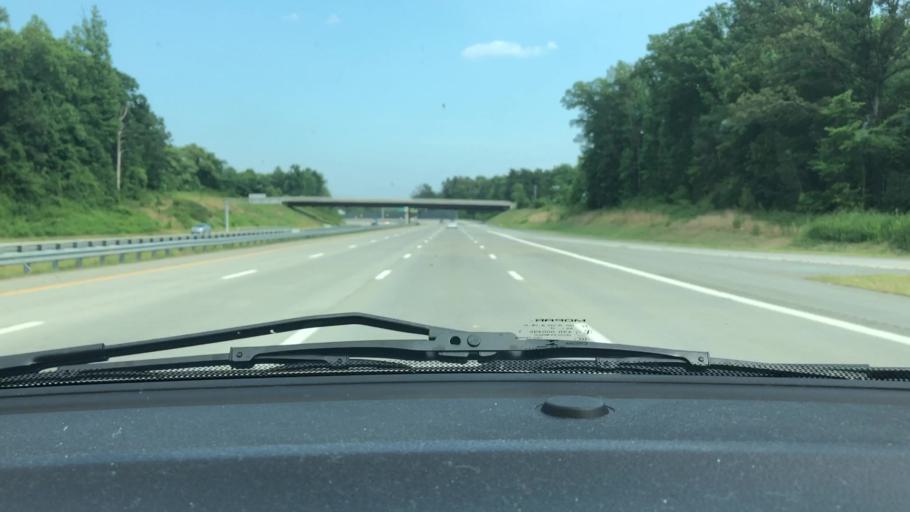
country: US
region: North Carolina
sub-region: Guilford County
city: Jamestown
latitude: 36.0244
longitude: -79.8809
